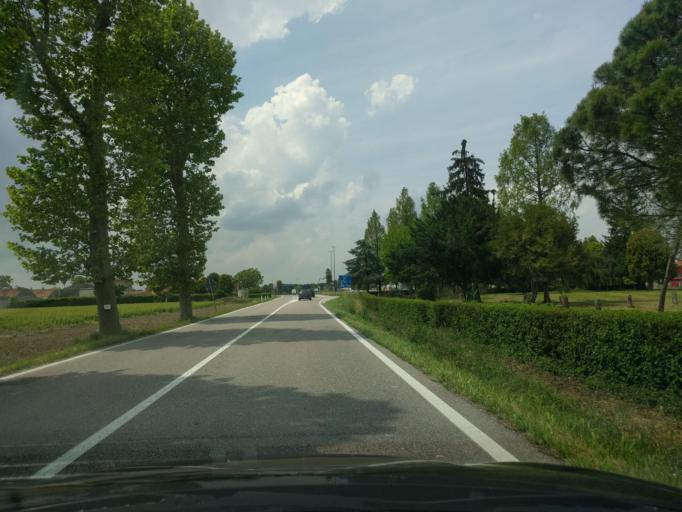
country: IT
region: Veneto
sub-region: Provincia di Rovigo
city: Villanova del Ghebbo Canton
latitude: 45.0756
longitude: 11.6592
